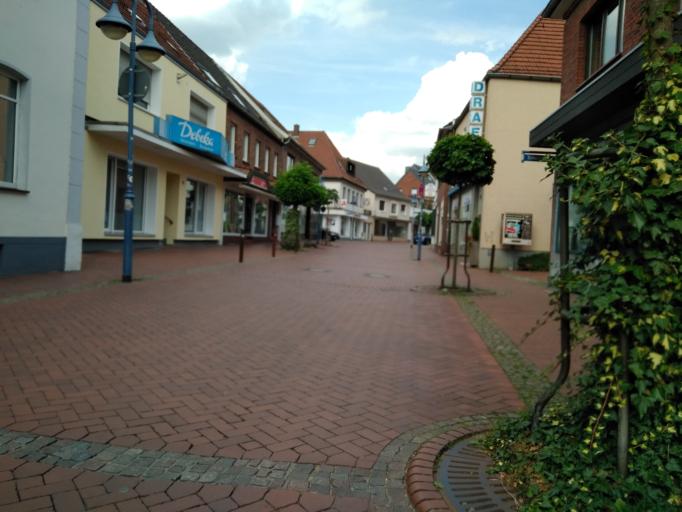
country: DE
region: North Rhine-Westphalia
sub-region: Regierungsbezirk Dusseldorf
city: Schermbeck
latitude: 51.6922
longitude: 6.8699
